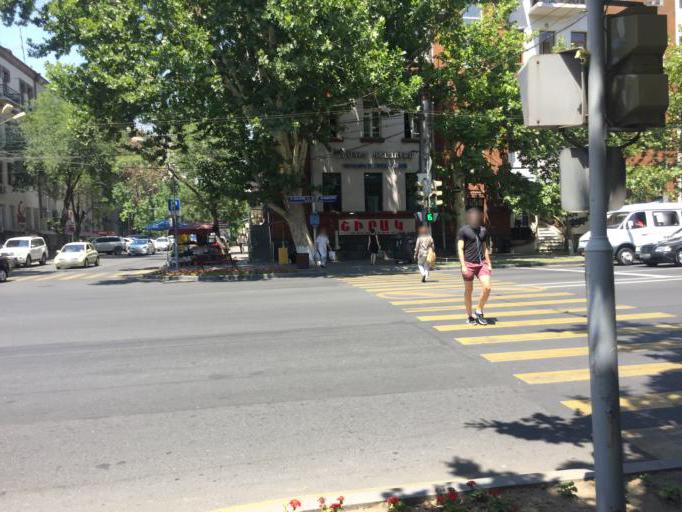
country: AM
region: Yerevan
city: Yerevan
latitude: 40.1837
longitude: 44.5113
